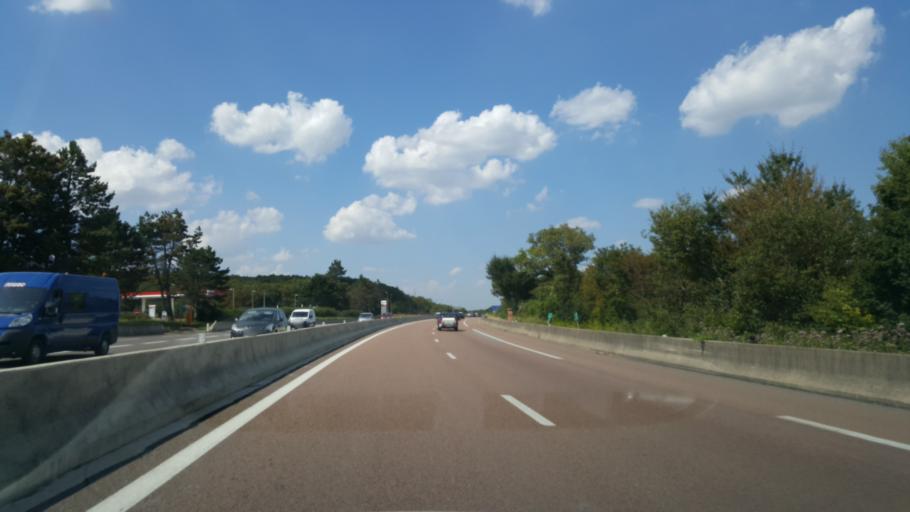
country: FR
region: Bourgogne
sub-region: Departement de la Cote-d'Or
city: Savigny-les-Beaune
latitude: 47.1043
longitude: 4.7155
